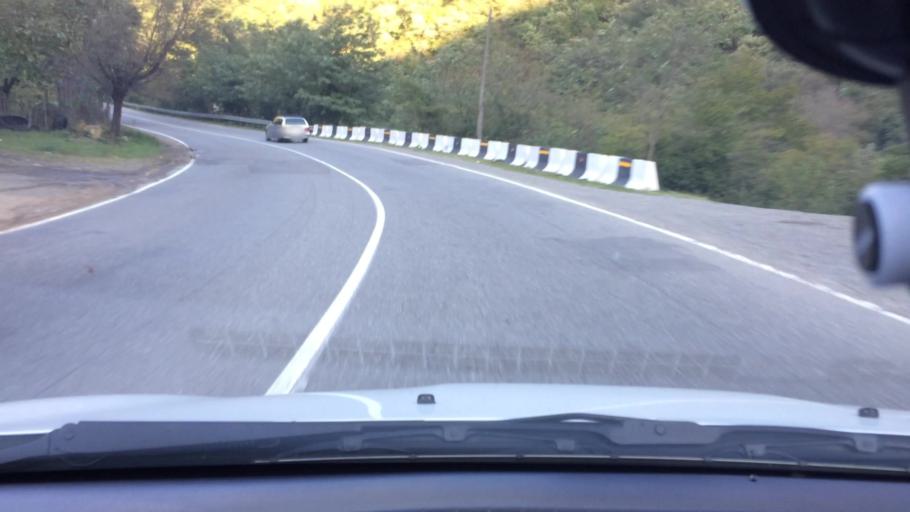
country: GE
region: Imereti
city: Kharagauli
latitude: 42.1101
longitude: 43.3626
